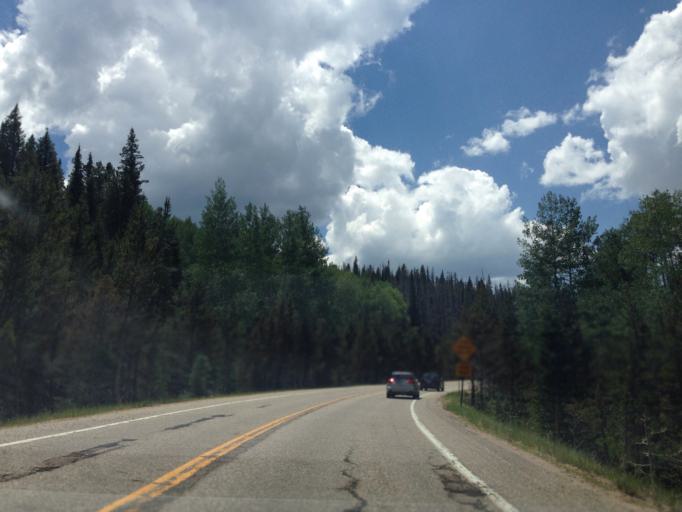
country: US
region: Colorado
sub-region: Larimer County
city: Estes Park
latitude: 40.6127
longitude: -105.8249
